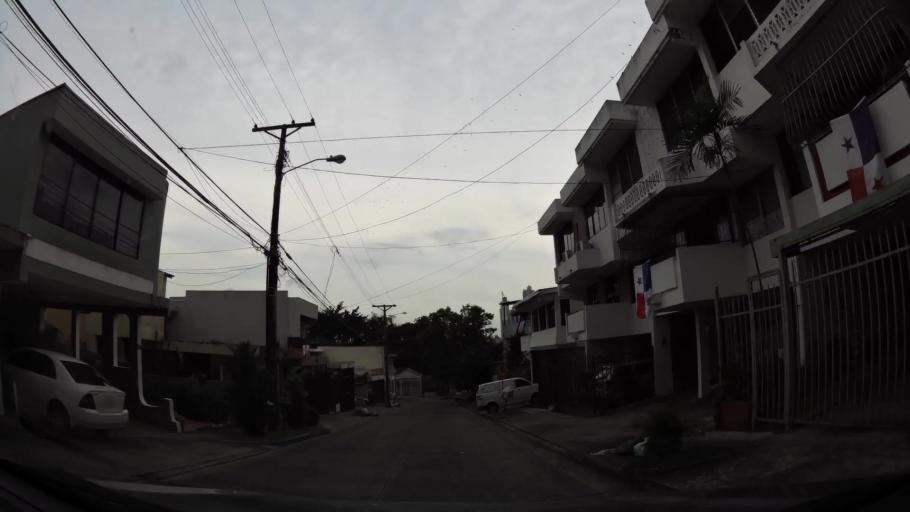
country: PA
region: Panama
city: Panama
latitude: 9.0131
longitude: -79.5327
